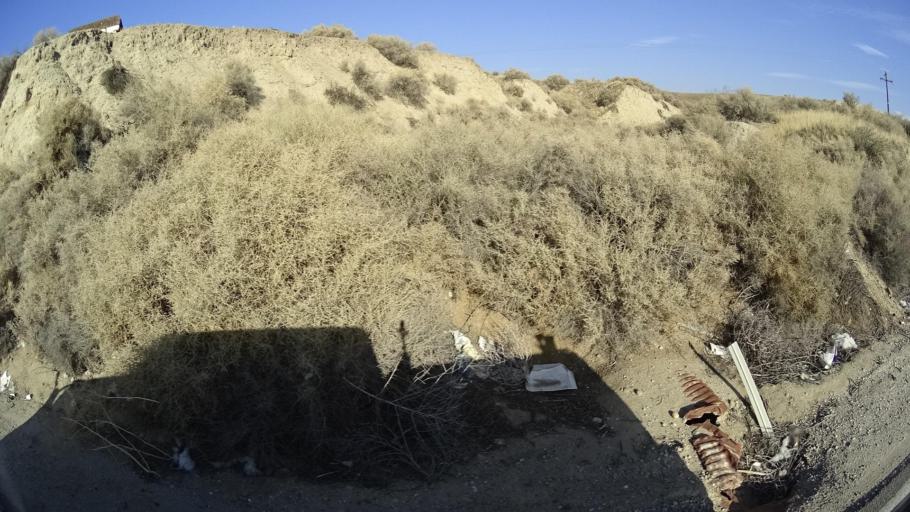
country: US
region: California
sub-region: Kern County
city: Oildale
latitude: 35.4512
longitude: -118.9052
